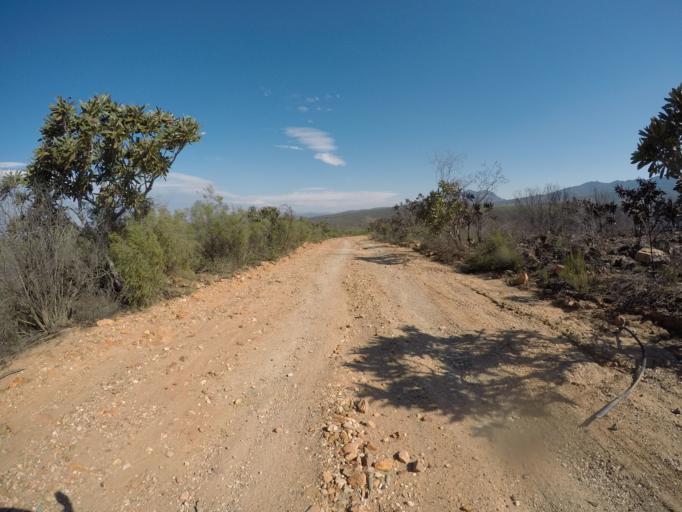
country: ZA
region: Eastern Cape
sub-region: Cacadu District Municipality
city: Kareedouw
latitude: -33.6366
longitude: 24.4525
